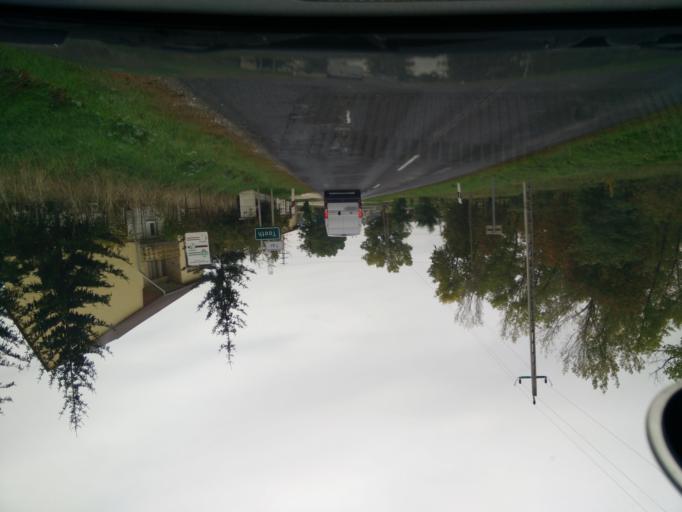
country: HU
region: Komarom-Esztergom
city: Tat
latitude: 47.7375
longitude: 18.6514
